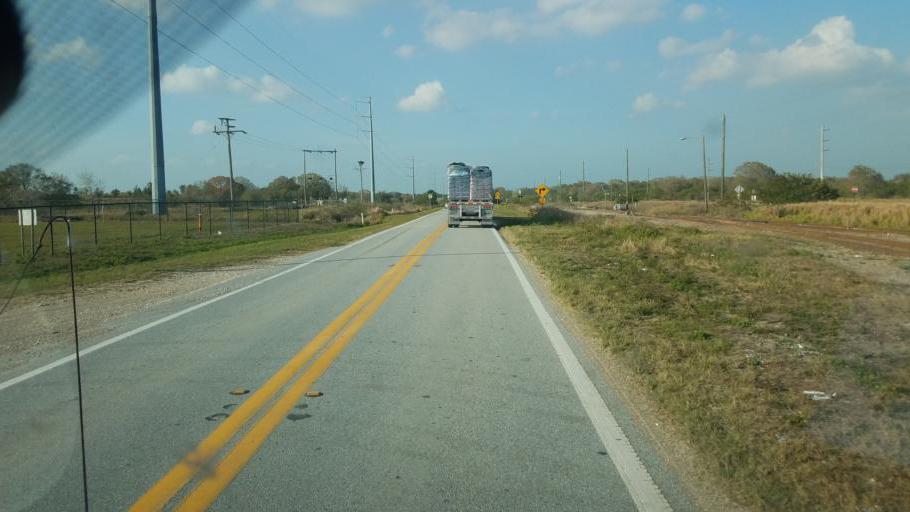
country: US
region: Florida
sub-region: Hardee County
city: Bowling Green
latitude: 27.6861
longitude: -81.9560
